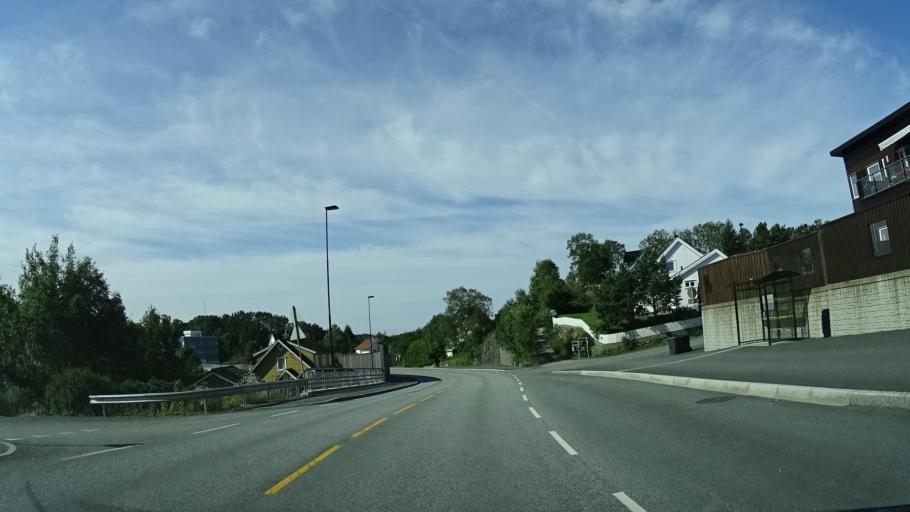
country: NO
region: Hordaland
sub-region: Stord
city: Sagvag
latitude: 59.7783
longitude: 5.3963
